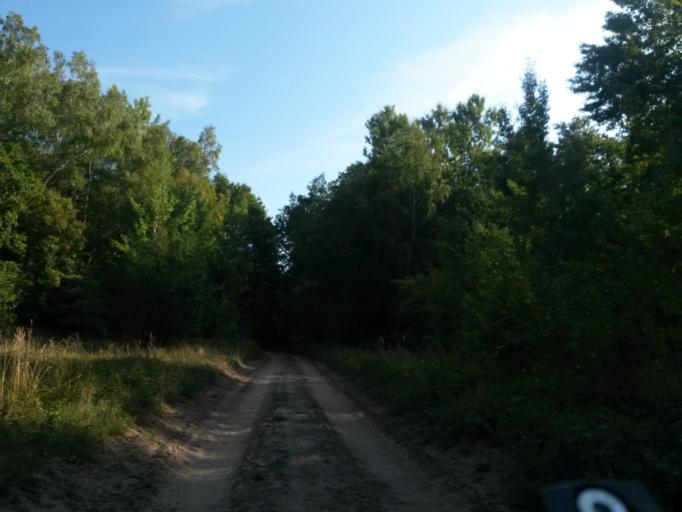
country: DE
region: Saxony-Anhalt
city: Nudersdorf
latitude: 51.9019
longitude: 12.5797
